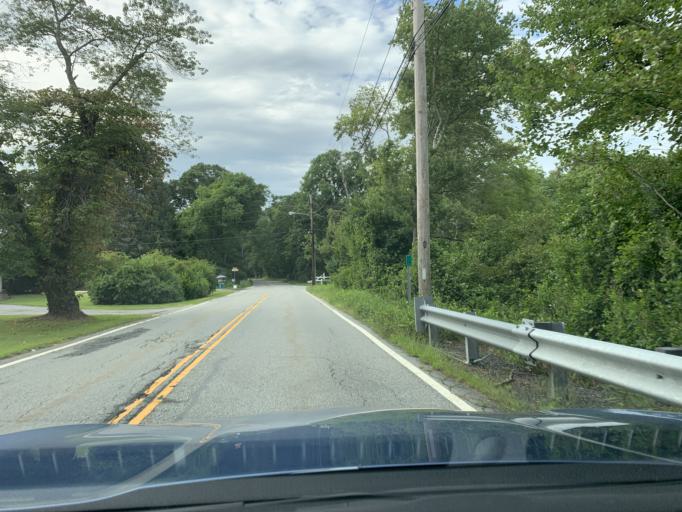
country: US
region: Rhode Island
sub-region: Kent County
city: East Greenwich
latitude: 41.6227
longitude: -71.4462
